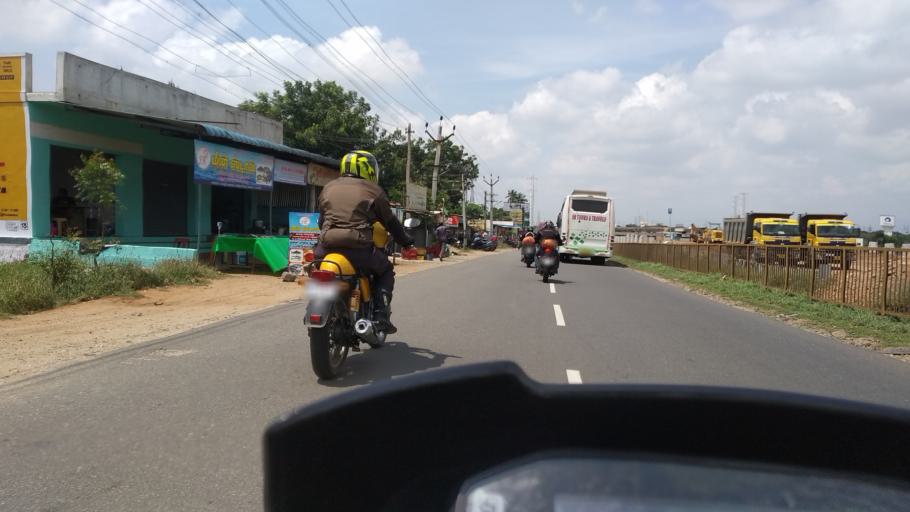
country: IN
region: Tamil Nadu
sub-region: Coimbatore
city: Sulur
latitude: 11.0906
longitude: 77.1382
